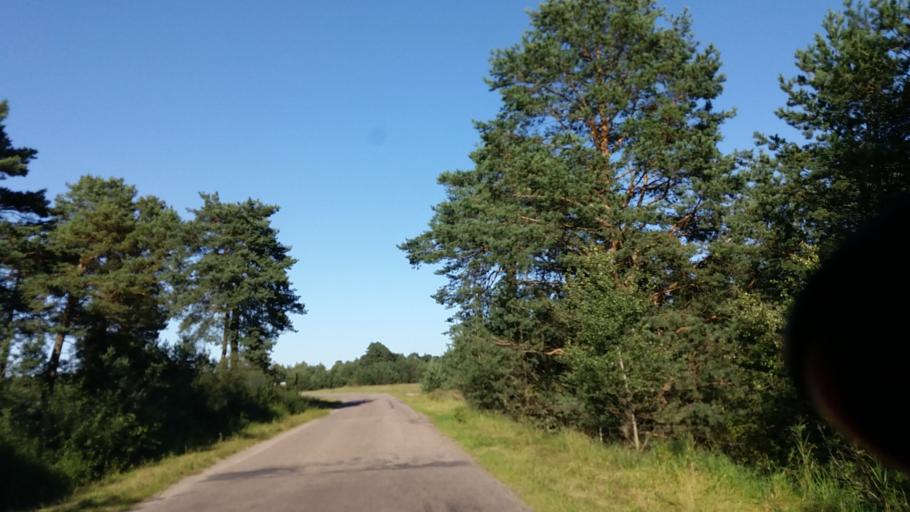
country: PL
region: West Pomeranian Voivodeship
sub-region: Powiat szczecinecki
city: Borne Sulinowo
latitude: 53.5734
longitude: 16.5302
